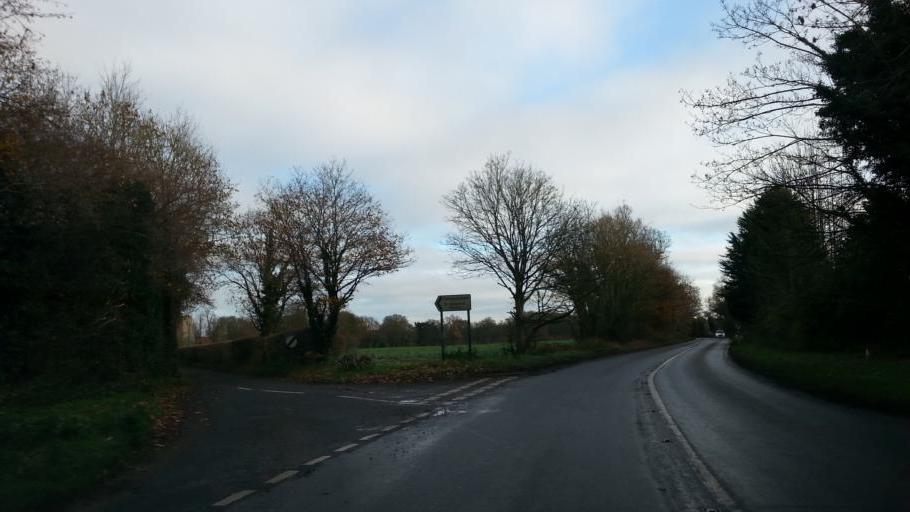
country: GB
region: England
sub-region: Suffolk
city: Wickham Market
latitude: 52.1218
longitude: 1.3914
